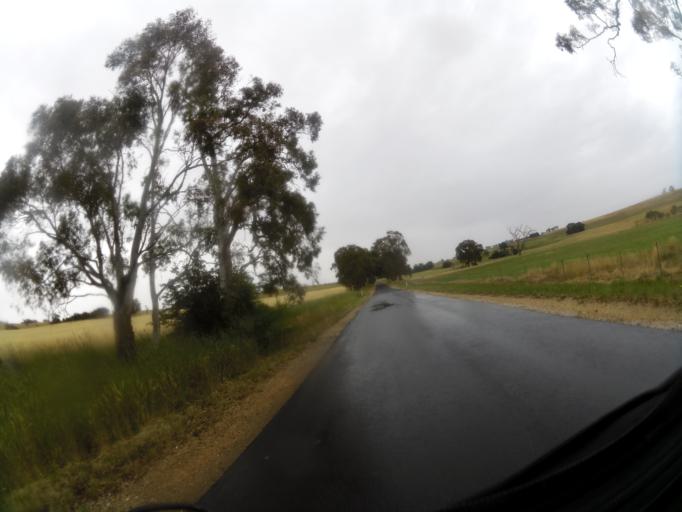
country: AU
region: Victoria
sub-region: Mount Alexander
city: Castlemaine
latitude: -37.2511
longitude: 144.0292
